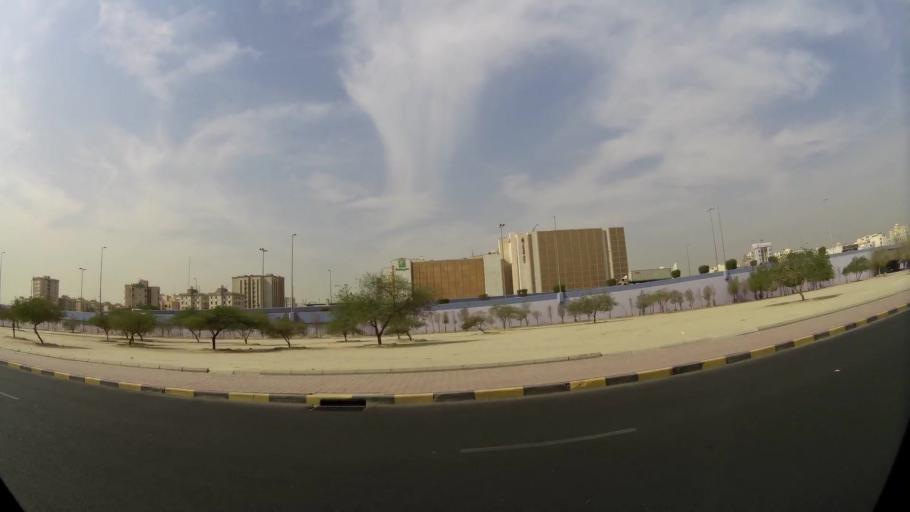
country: KW
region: Al Farwaniyah
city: Janub as Surrah
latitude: 29.2709
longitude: 47.9706
